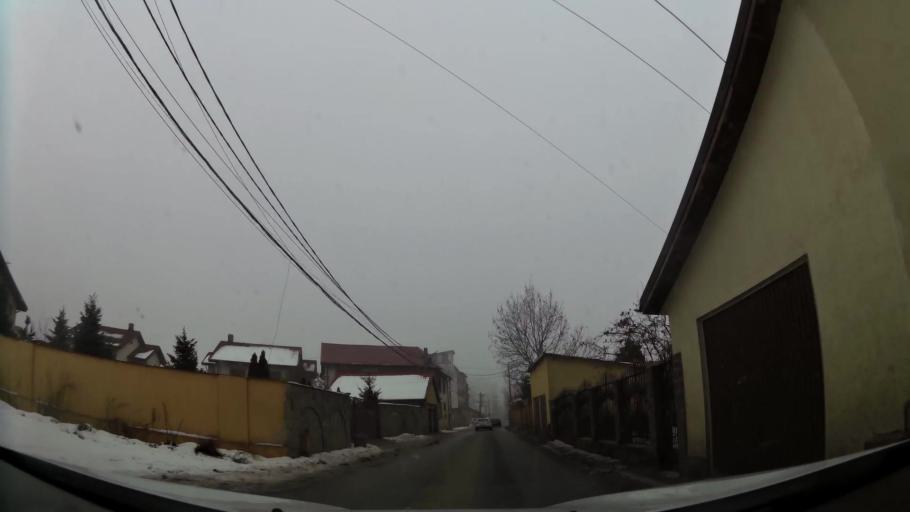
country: RO
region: Ilfov
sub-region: Comuna Chiajna
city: Rosu
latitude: 44.4508
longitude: 25.9930
